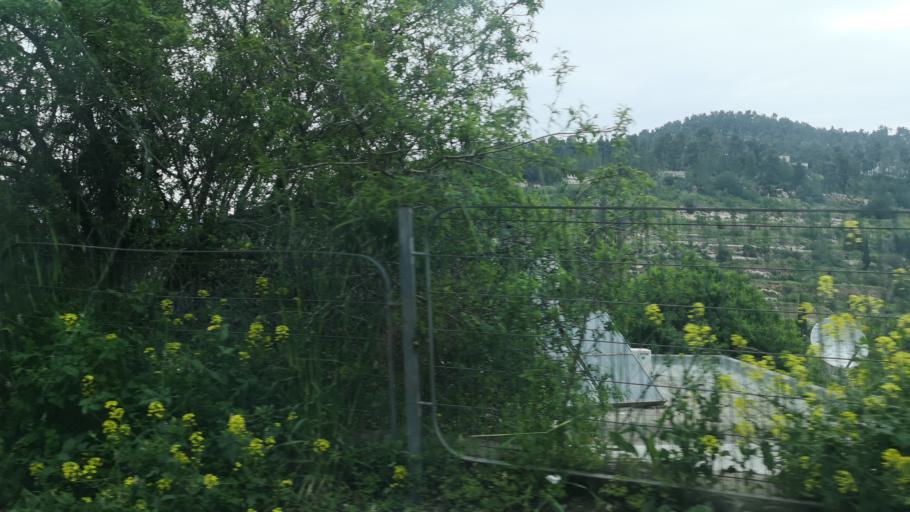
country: PS
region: West Bank
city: Bayt Iksa
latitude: 31.7693
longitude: 35.1617
